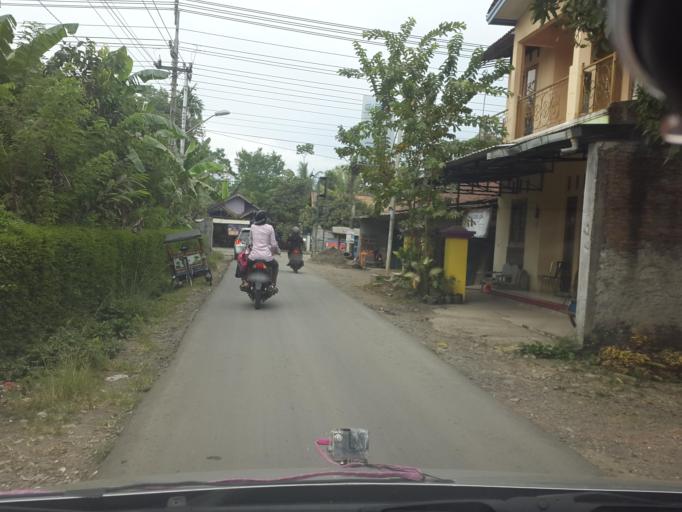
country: ID
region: Central Java
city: Gerduren
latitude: -7.5283
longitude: 109.0919
